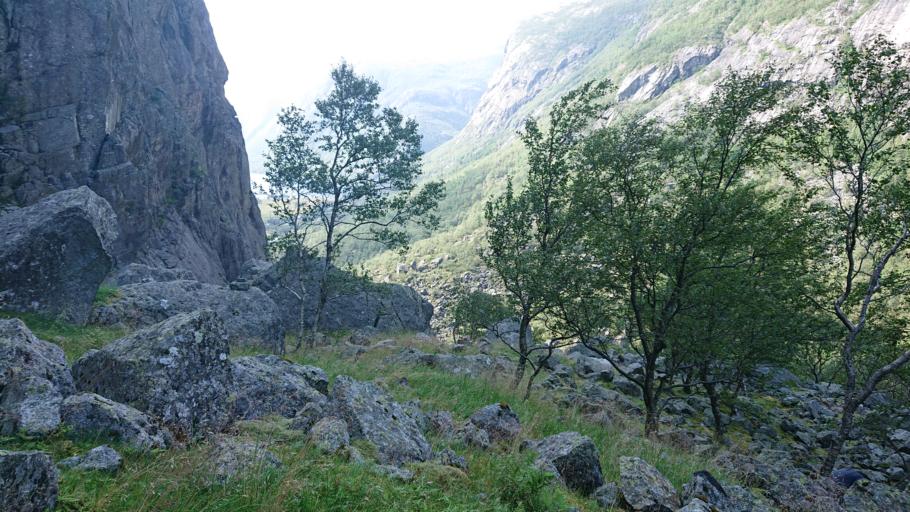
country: NO
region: Rogaland
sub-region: Hjelmeland
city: Hjelmelandsvagen
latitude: 59.1994
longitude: 6.4569
